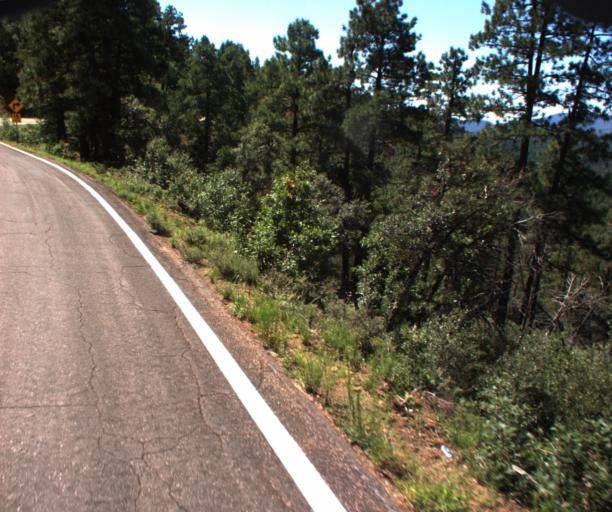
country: US
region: Arizona
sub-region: Greenlee County
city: Morenci
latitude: 33.5368
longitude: -109.3088
